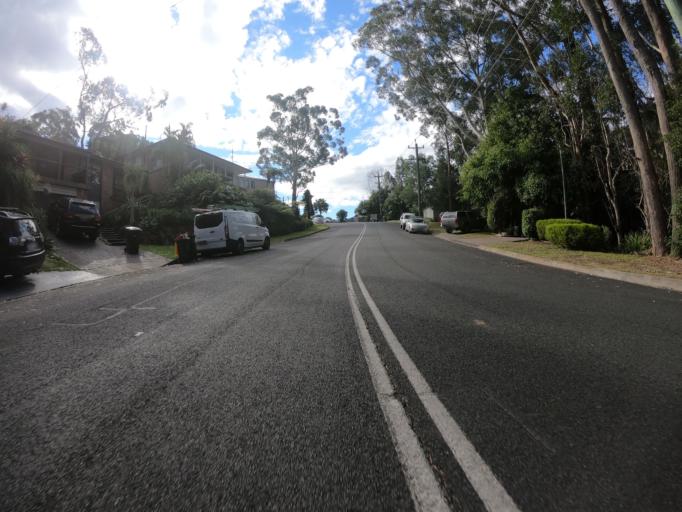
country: AU
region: New South Wales
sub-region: Wollongong
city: Bulli
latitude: -34.3325
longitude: 150.9026
